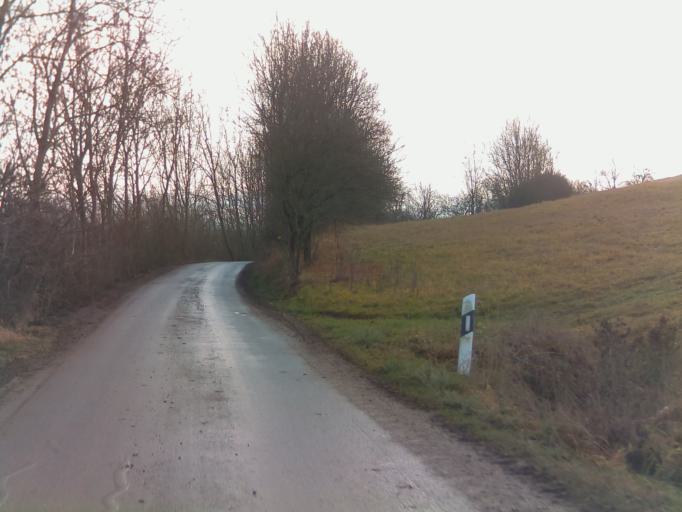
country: DE
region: Thuringia
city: Gumperda
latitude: 50.7975
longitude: 11.5141
